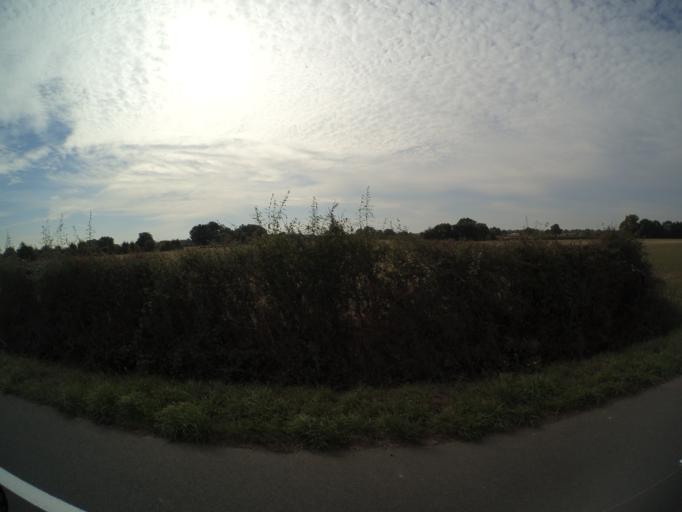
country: FR
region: Pays de la Loire
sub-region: Departement de Maine-et-Loire
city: Chemille-Melay
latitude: 47.2133
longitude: -0.7874
